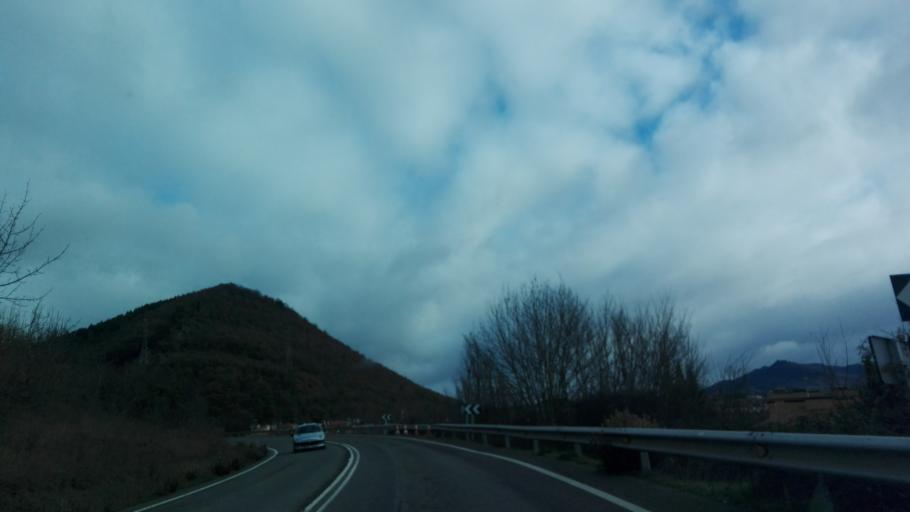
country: ES
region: Navarre
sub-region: Provincia de Navarra
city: Atarrabia
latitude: 42.8350
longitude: -1.6071
